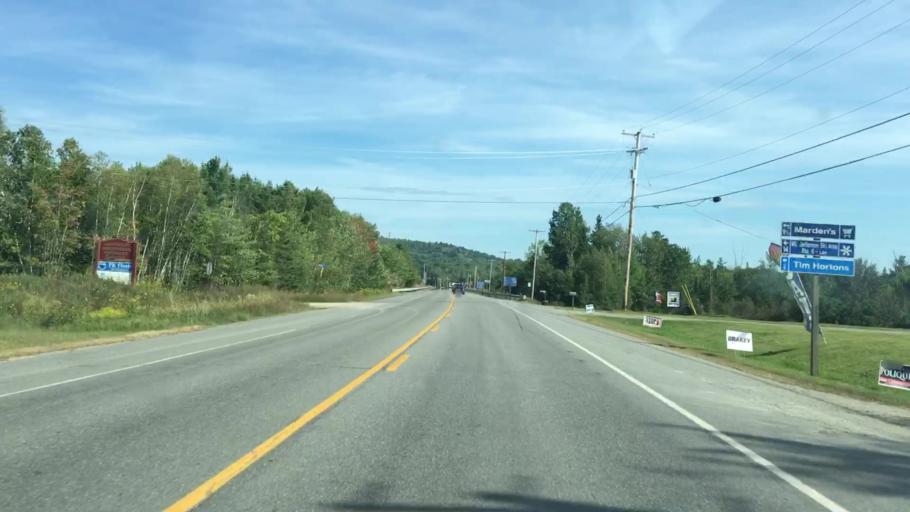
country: US
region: Maine
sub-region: Penobscot County
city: Lincoln
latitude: 45.3568
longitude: -68.5399
